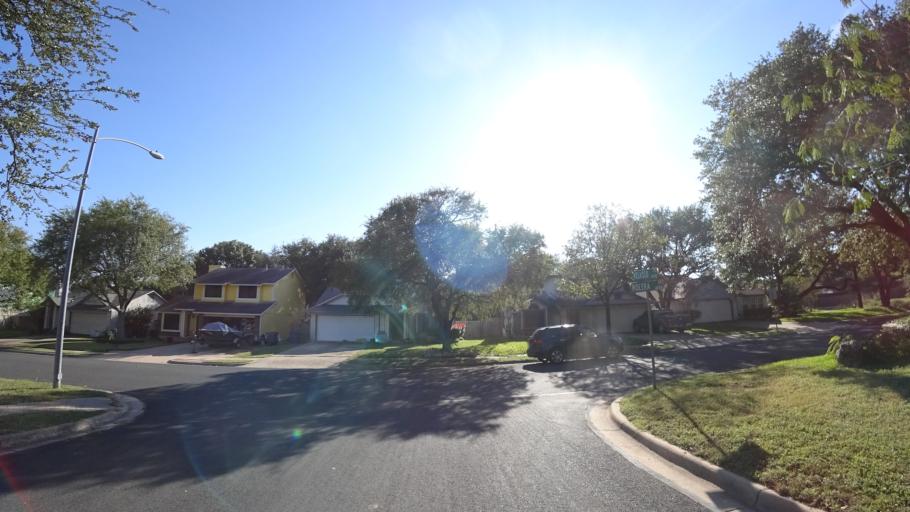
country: US
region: Texas
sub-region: Travis County
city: Shady Hollow
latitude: 30.2084
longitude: -97.8542
